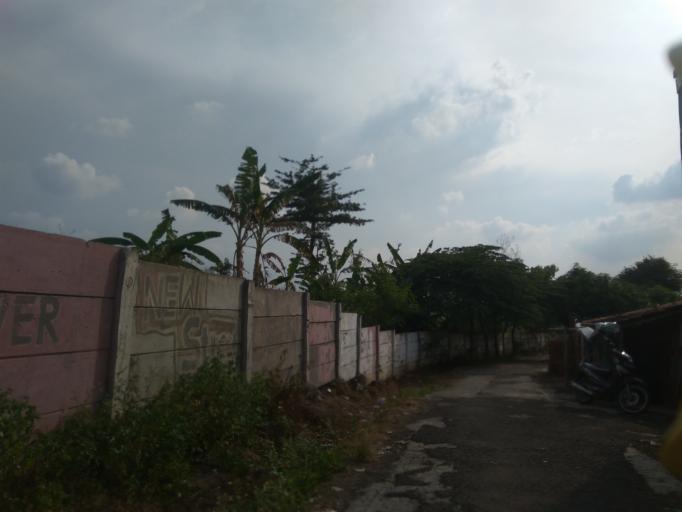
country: ID
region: Central Java
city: Semarang
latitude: -7.0208
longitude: 110.4453
